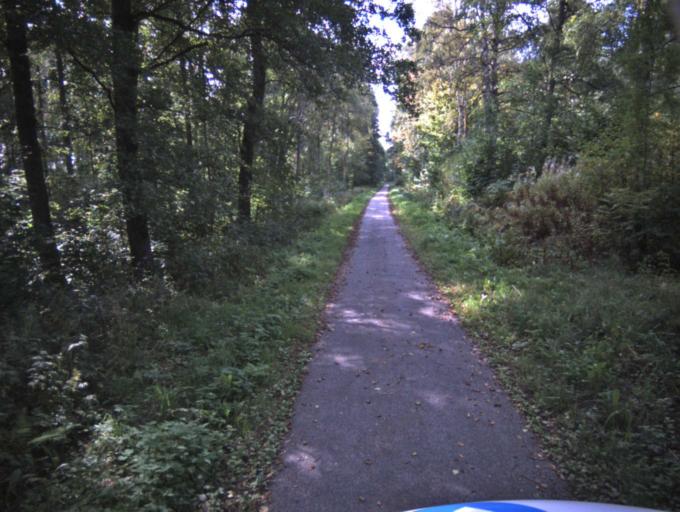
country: SE
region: Vaestra Goetaland
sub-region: Tranemo Kommun
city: Limmared
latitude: 57.6423
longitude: 13.3582
